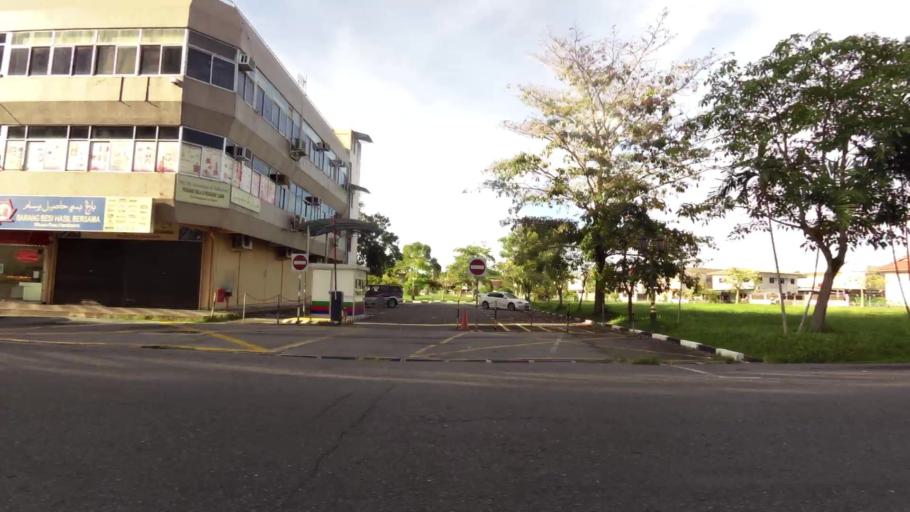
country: BN
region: Belait
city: Kuala Belait
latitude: 4.5834
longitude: 114.1929
